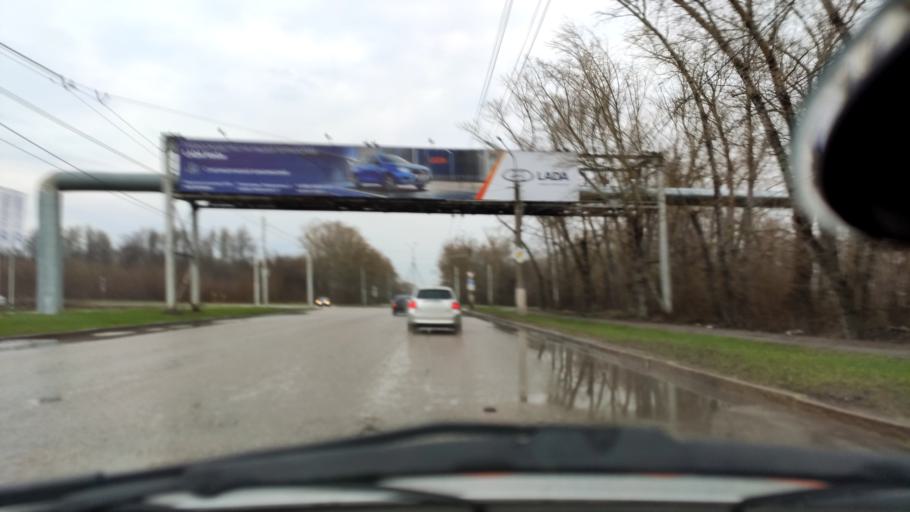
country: RU
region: Bashkortostan
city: Sterlitamak
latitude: 53.6554
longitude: 55.9486
